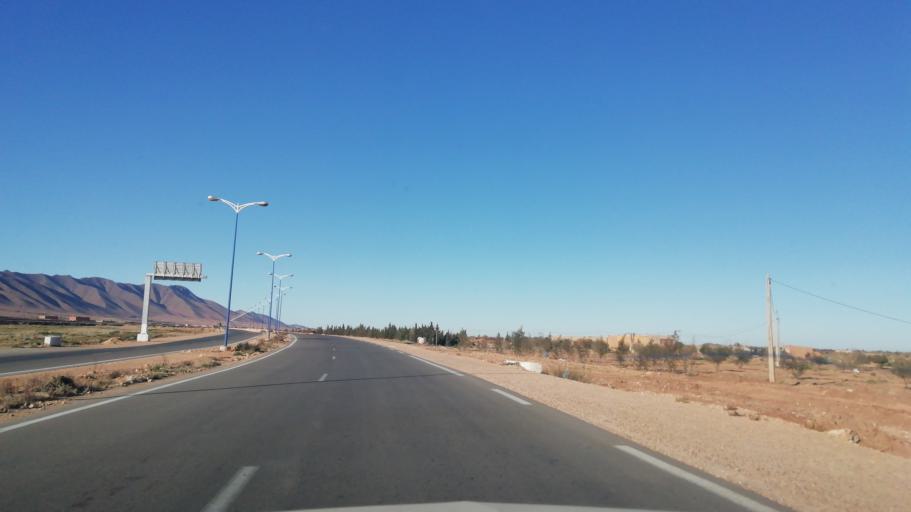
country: DZ
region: Wilaya de Naama
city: Naama
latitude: 33.5599
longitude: -0.2370
